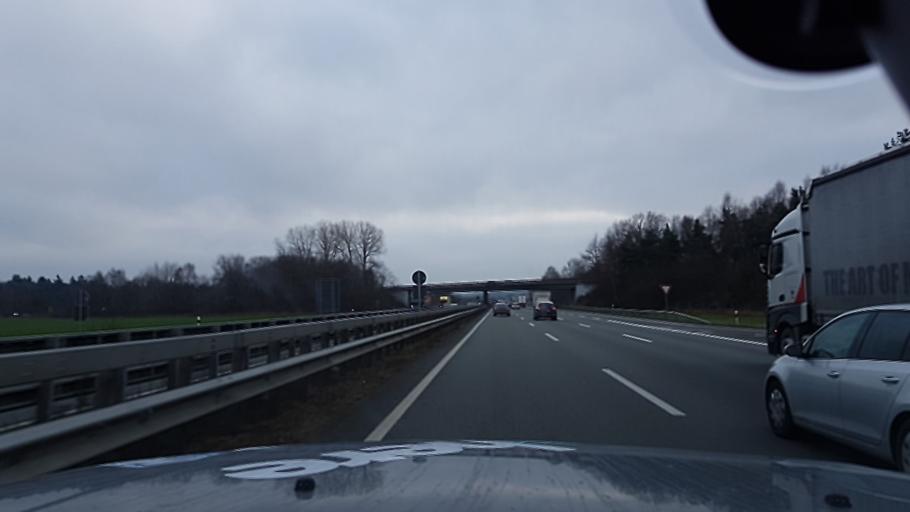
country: DE
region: Lower Saxony
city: Wallenhorst
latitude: 52.3965
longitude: 8.0373
